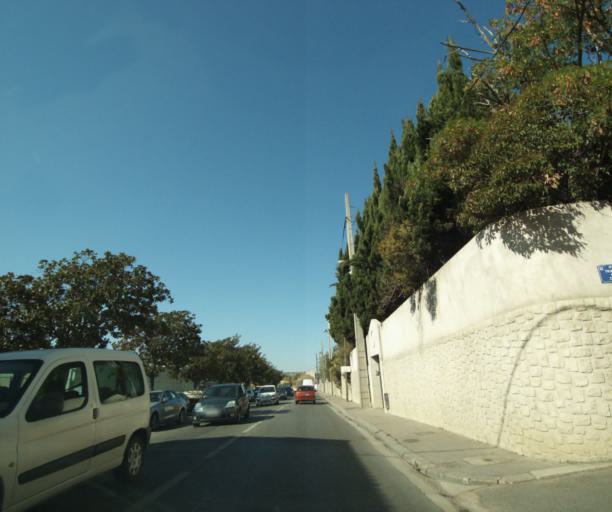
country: FR
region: Provence-Alpes-Cote d'Azur
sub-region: Departement des Bouches-du-Rhone
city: Marseille 14
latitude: 43.3374
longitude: 5.3958
